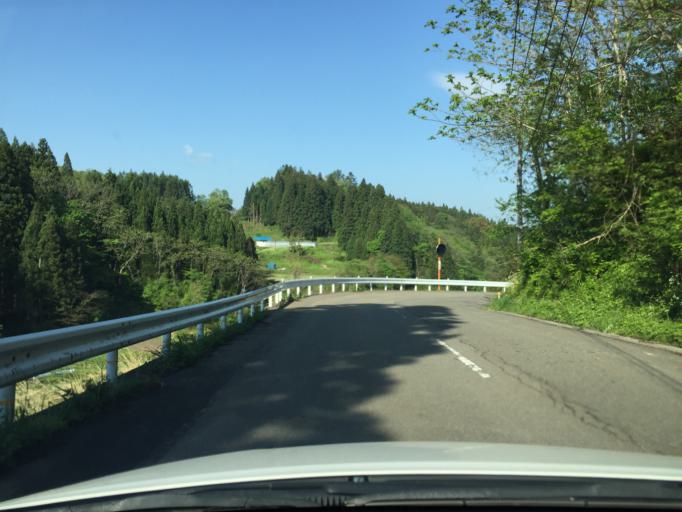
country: JP
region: Fukushima
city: Kitakata
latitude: 37.6833
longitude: 139.6791
